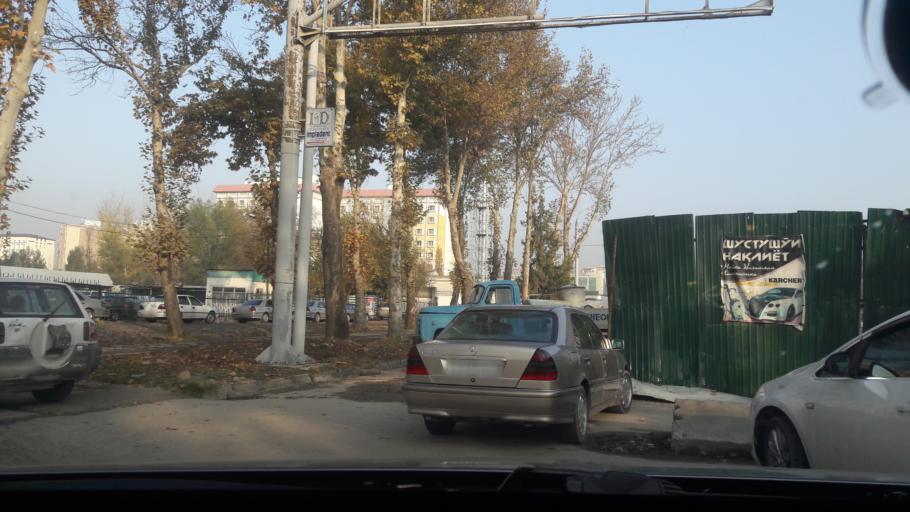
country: TJ
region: Dushanbe
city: Dushanbe
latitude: 38.5810
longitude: 68.7550
